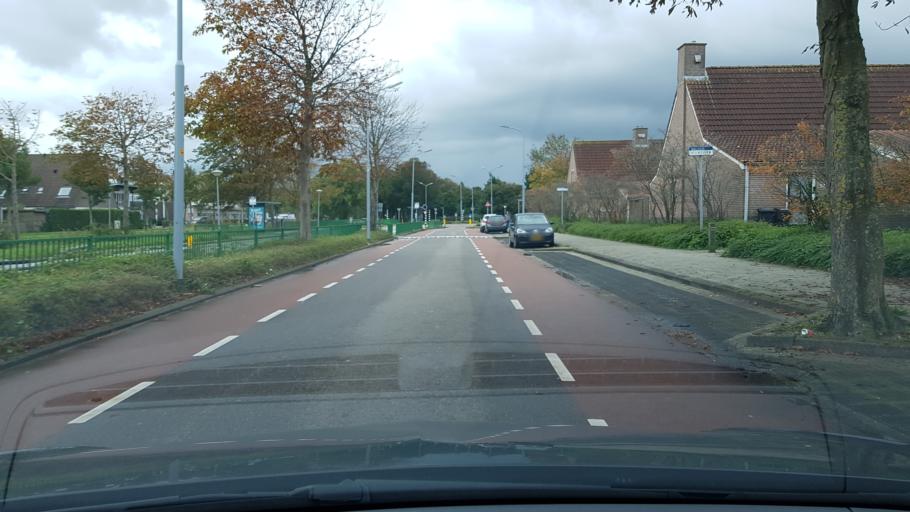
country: NL
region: North Holland
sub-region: Gemeente Haarlemmermeer
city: Hoofddorp
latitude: 52.3163
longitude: 4.6572
